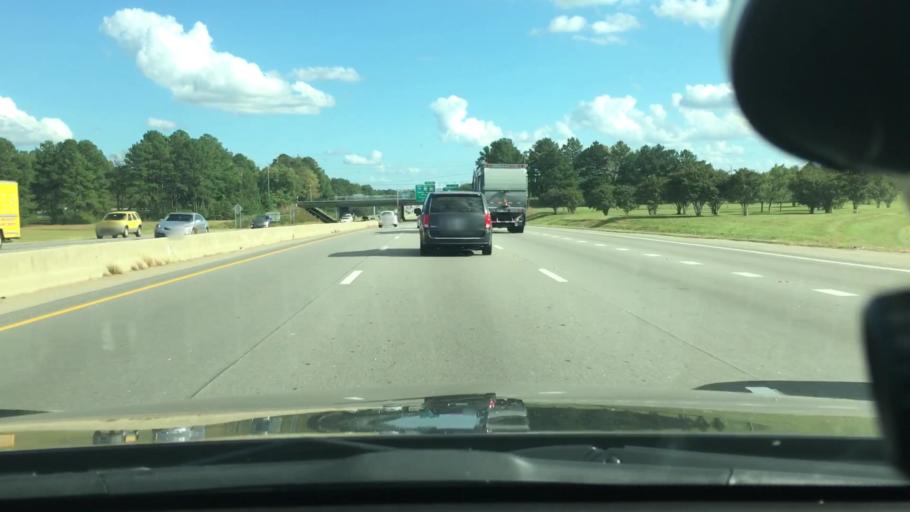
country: US
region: North Carolina
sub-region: Wake County
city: Raleigh
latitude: 35.7961
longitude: -78.5850
